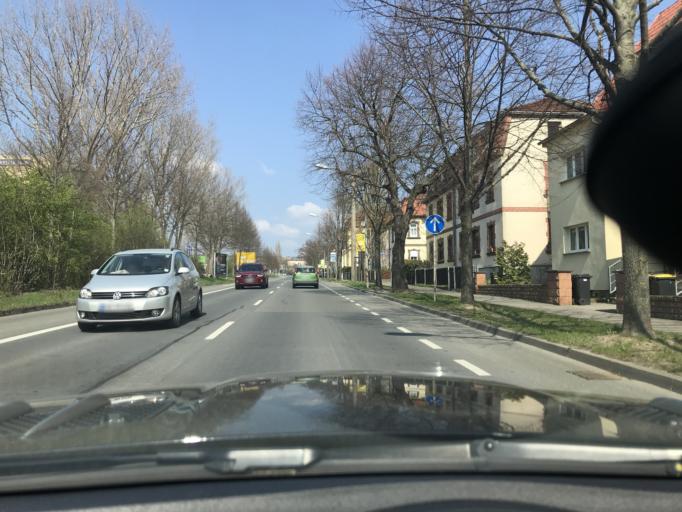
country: DE
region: Thuringia
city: Weimar
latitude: 50.9964
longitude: 11.3325
